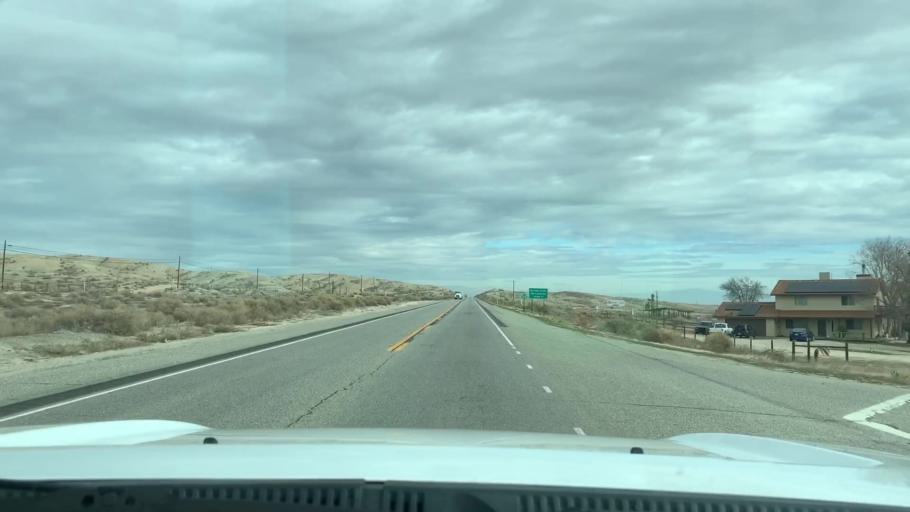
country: US
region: California
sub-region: Kern County
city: Ford City
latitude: 35.2323
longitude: -119.3712
